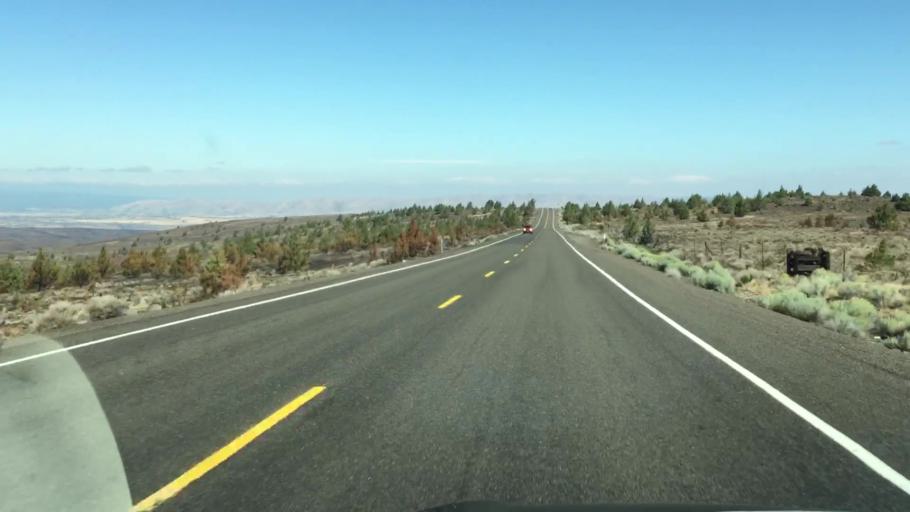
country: US
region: Oregon
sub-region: Jefferson County
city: Warm Springs
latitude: 45.0780
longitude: -121.0243
